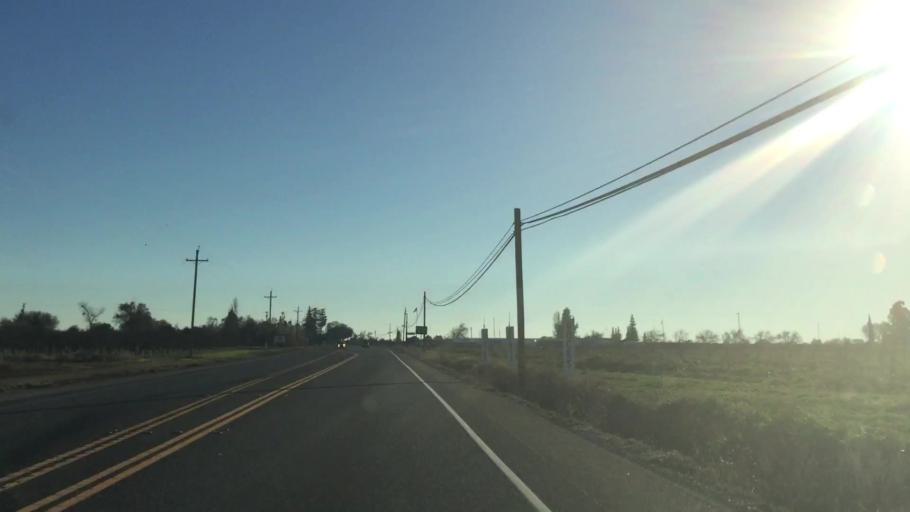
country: US
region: California
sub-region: Sutter County
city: Live Oak
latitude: 39.2588
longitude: -121.5984
